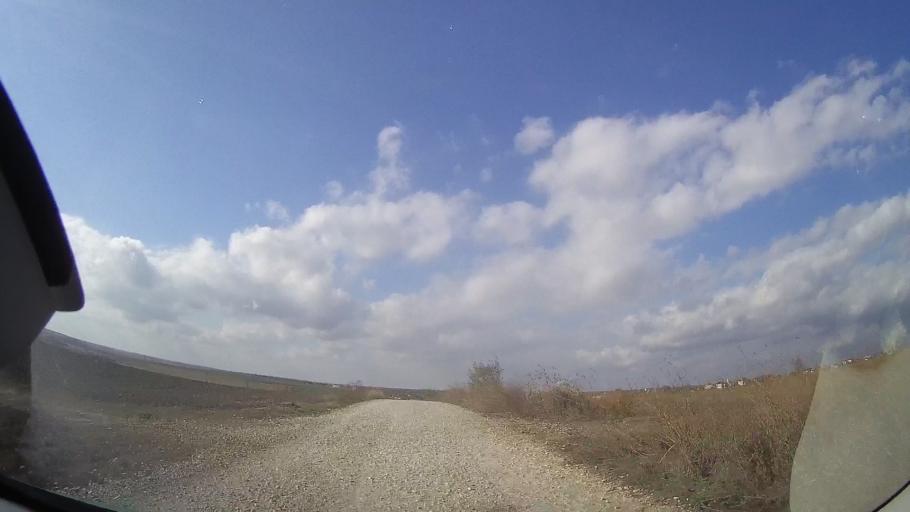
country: RO
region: Constanta
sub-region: Comuna Douazeci si Trei August
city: Douazeci si Trei August
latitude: 43.9111
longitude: 28.5963
